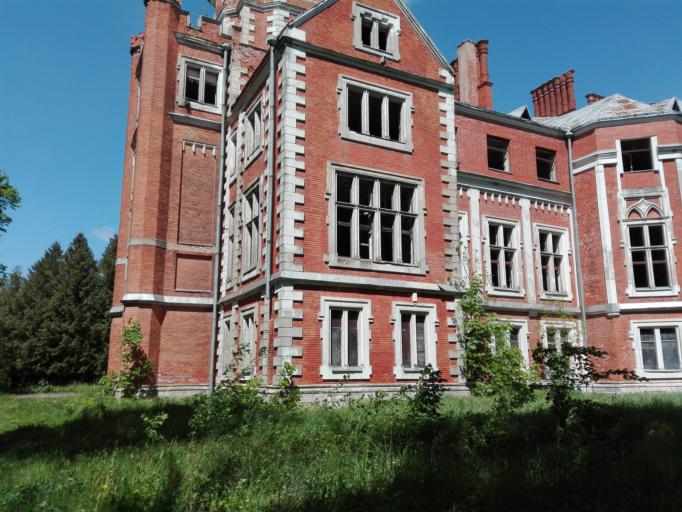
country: LT
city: Lentvaris
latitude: 54.6581
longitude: 25.0397
